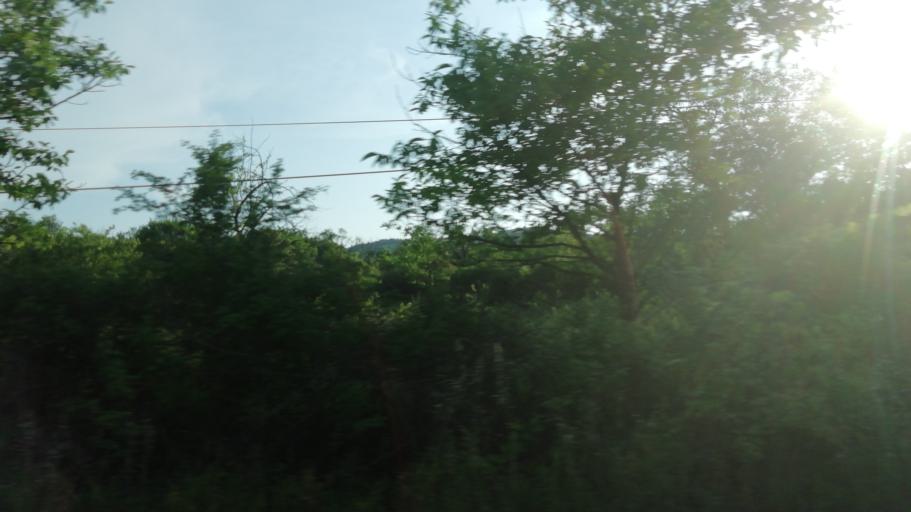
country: TR
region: Karabuk
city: Karabuk
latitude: 41.1396
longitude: 32.6309
